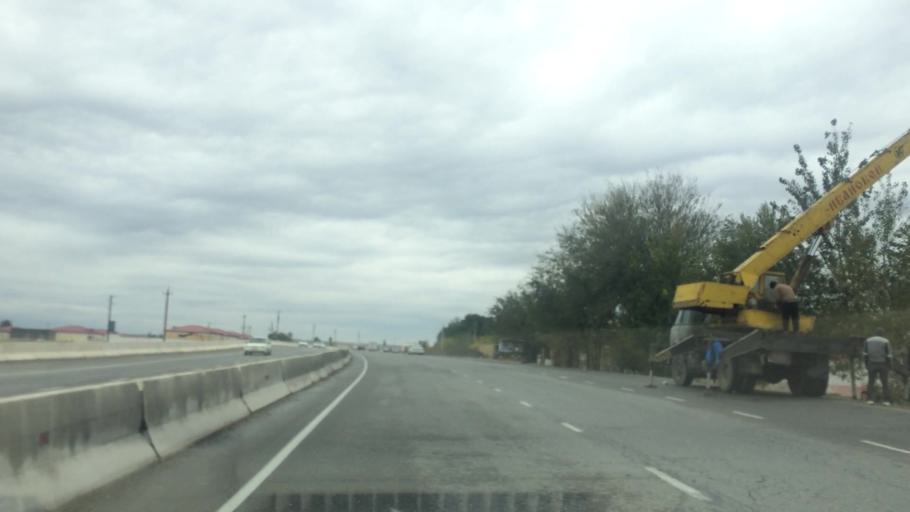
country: UZ
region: Jizzax
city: Jizzax
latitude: 39.9757
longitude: 67.5614
